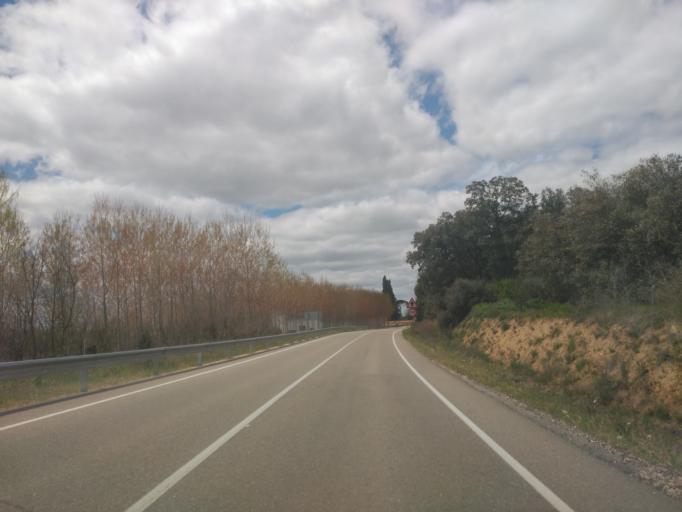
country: ES
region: Castille and Leon
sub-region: Provincia de Salamanca
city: Valverdon
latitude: 41.0398
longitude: -5.7518
